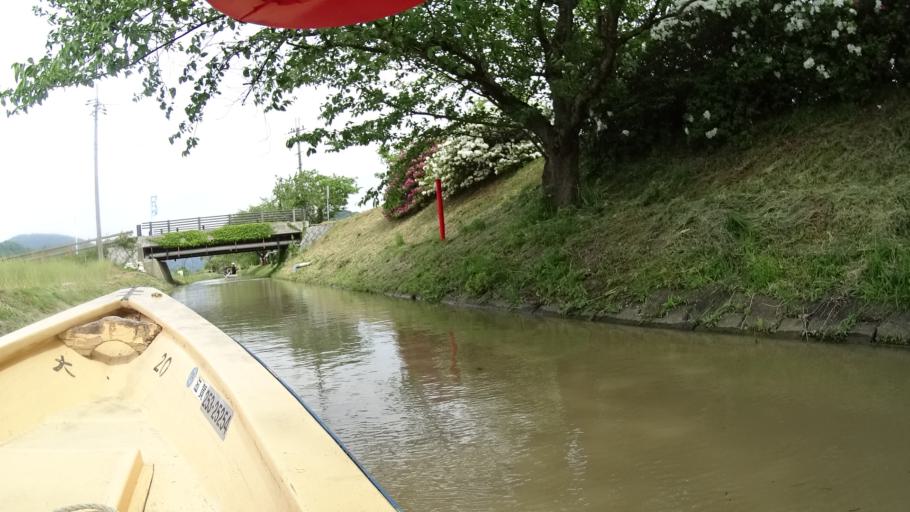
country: JP
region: Shiga Prefecture
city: Omihachiman
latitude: 35.1529
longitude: 136.1005
